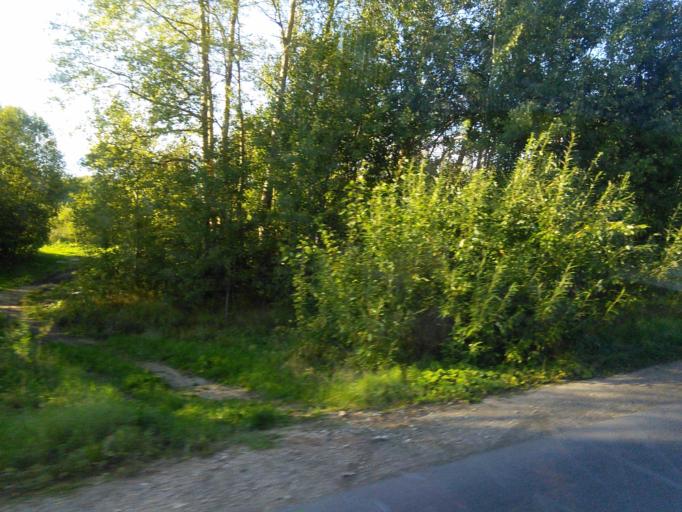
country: RU
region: Jaroslavl
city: Poshekhon'ye
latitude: 58.4951
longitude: 39.0955
